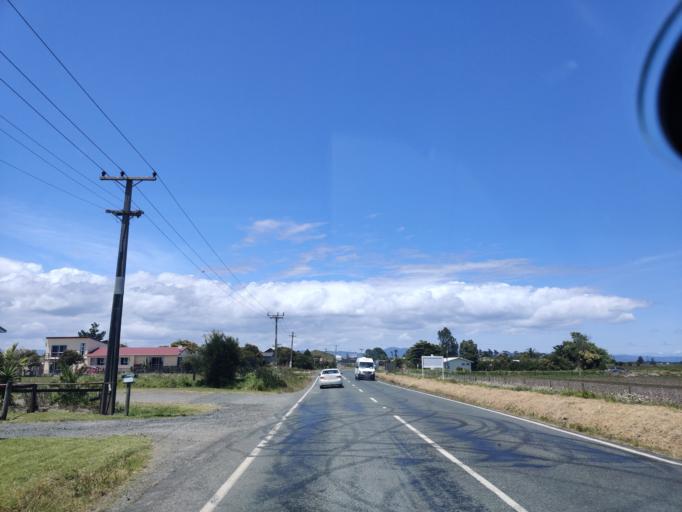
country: NZ
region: Northland
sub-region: Far North District
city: Kaitaia
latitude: -35.0349
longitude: 173.2544
